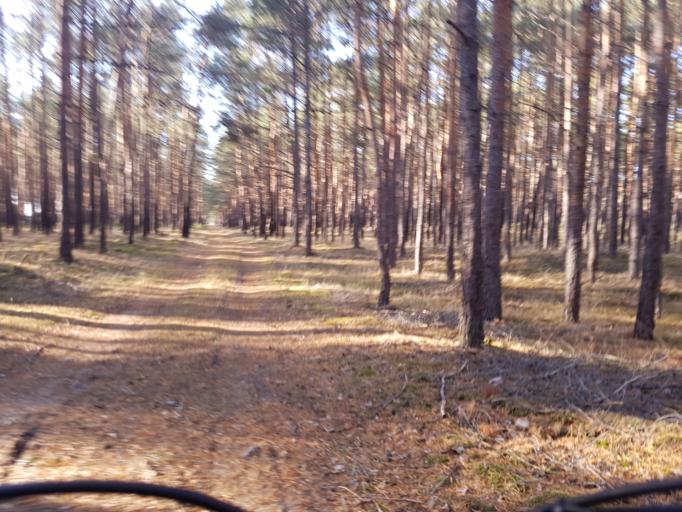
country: DE
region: Brandenburg
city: Schilda
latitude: 51.6149
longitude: 13.3805
